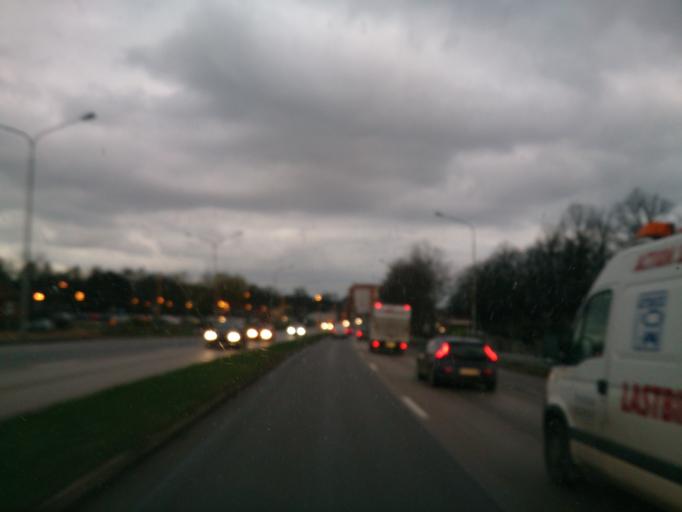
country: SE
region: OEstergoetland
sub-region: Linkopings Kommun
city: Linkoping
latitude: 58.4006
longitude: 15.6584
